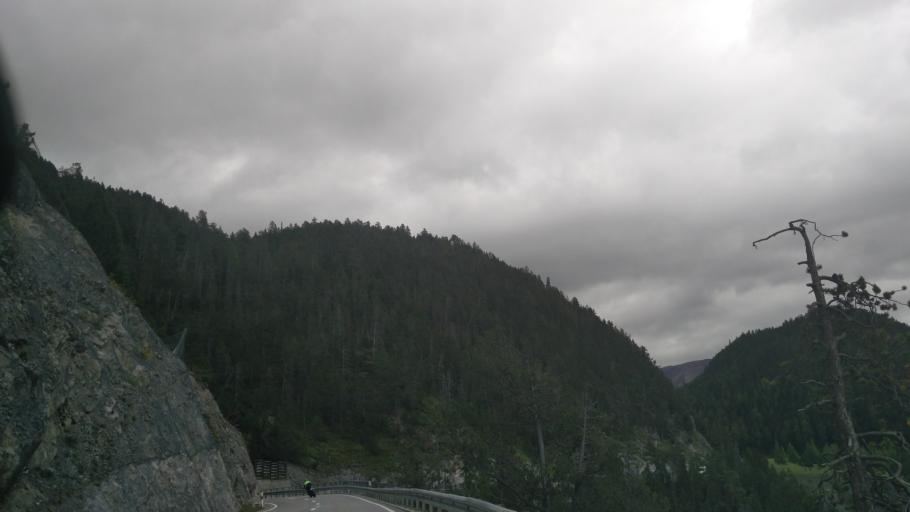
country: CH
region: Grisons
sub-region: Inn District
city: Zernez
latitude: 46.6891
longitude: 10.1423
